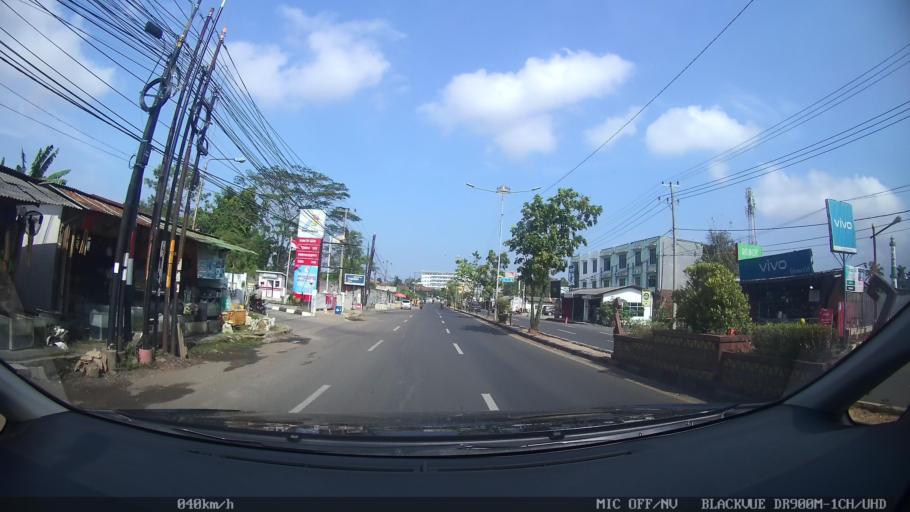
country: ID
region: Lampung
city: Kedaton
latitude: -5.3678
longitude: 105.2339
